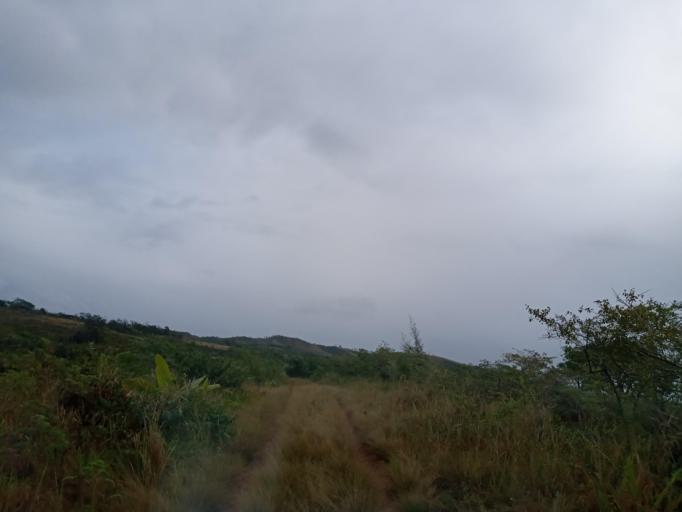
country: MG
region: Atsimo-Atsinanana
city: Vohipaho
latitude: -24.0051
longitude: 47.4105
